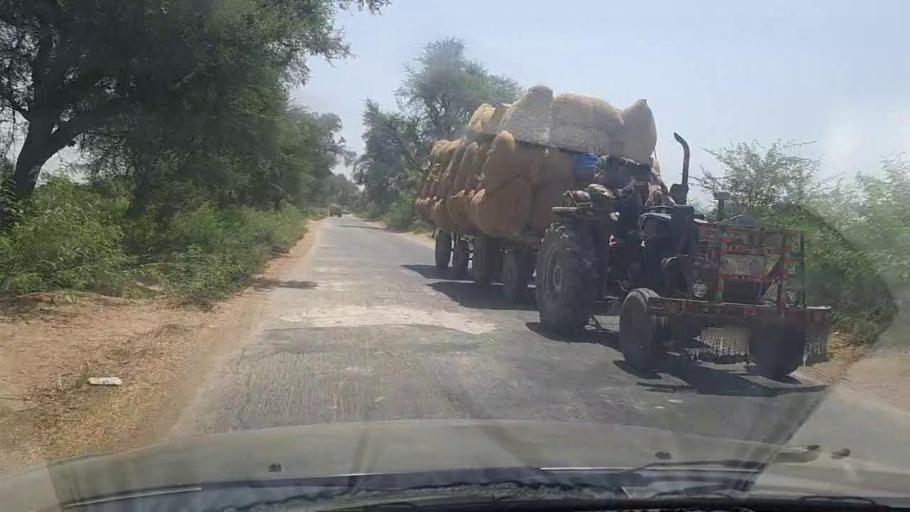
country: PK
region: Sindh
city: Tando Jam
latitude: 25.2835
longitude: 68.6012
